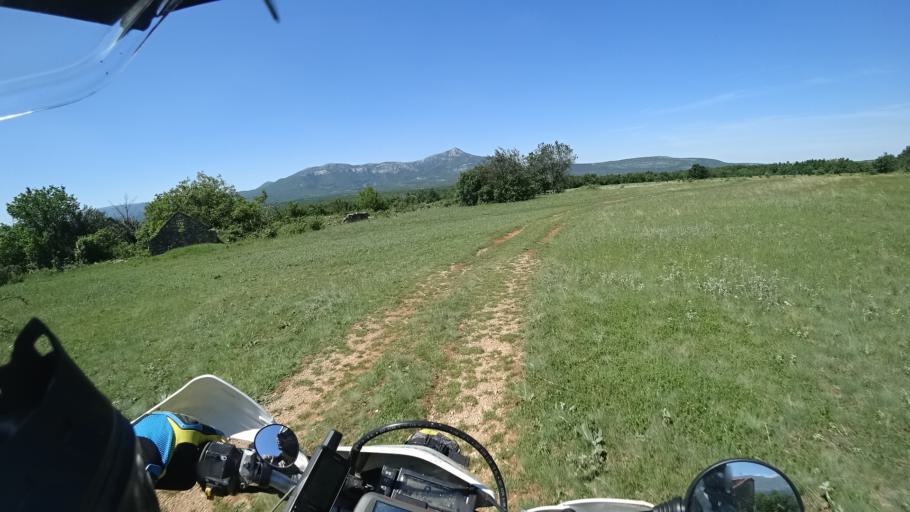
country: BA
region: Federation of Bosnia and Herzegovina
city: Bosansko Grahovo
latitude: 43.9969
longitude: 16.4125
